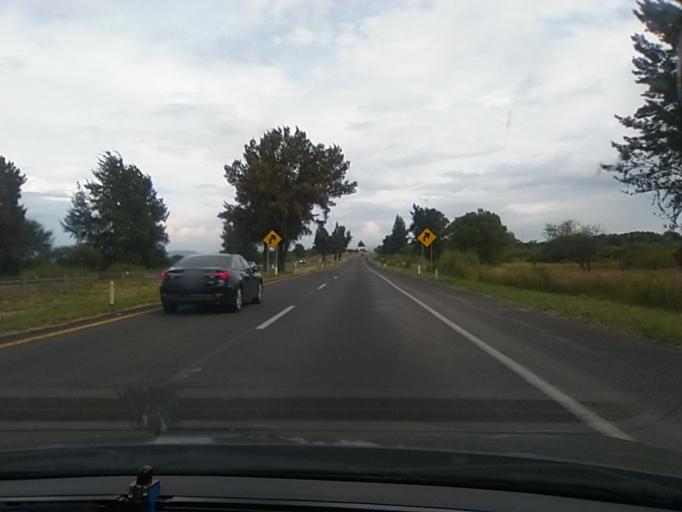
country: MX
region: Michoacan
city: Vistahermosa de Negrete
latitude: 20.2824
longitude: -102.4586
